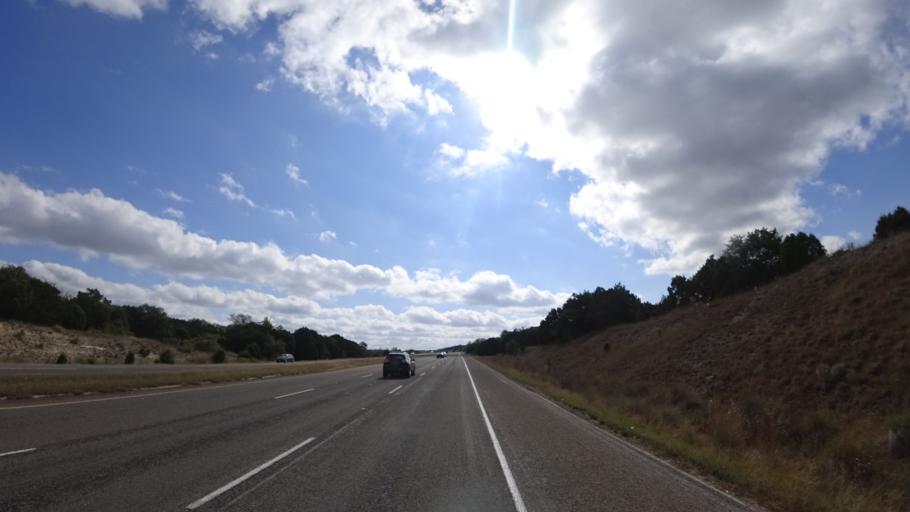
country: US
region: Texas
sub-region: Travis County
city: Barton Creek
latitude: 30.2750
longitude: -97.8981
